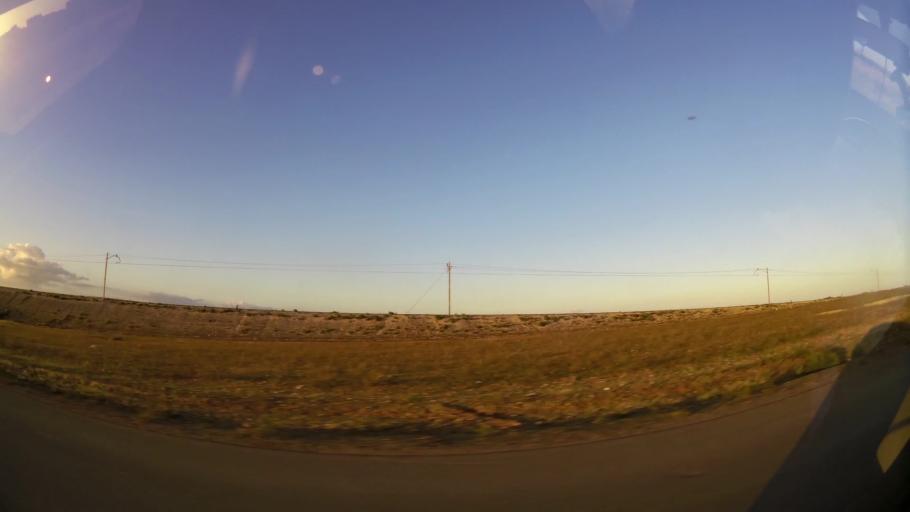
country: MA
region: Marrakech-Tensift-Al Haouz
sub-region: Kelaa-Des-Sraghna
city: Sidi Abdallah
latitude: 32.2390
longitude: -7.9291
